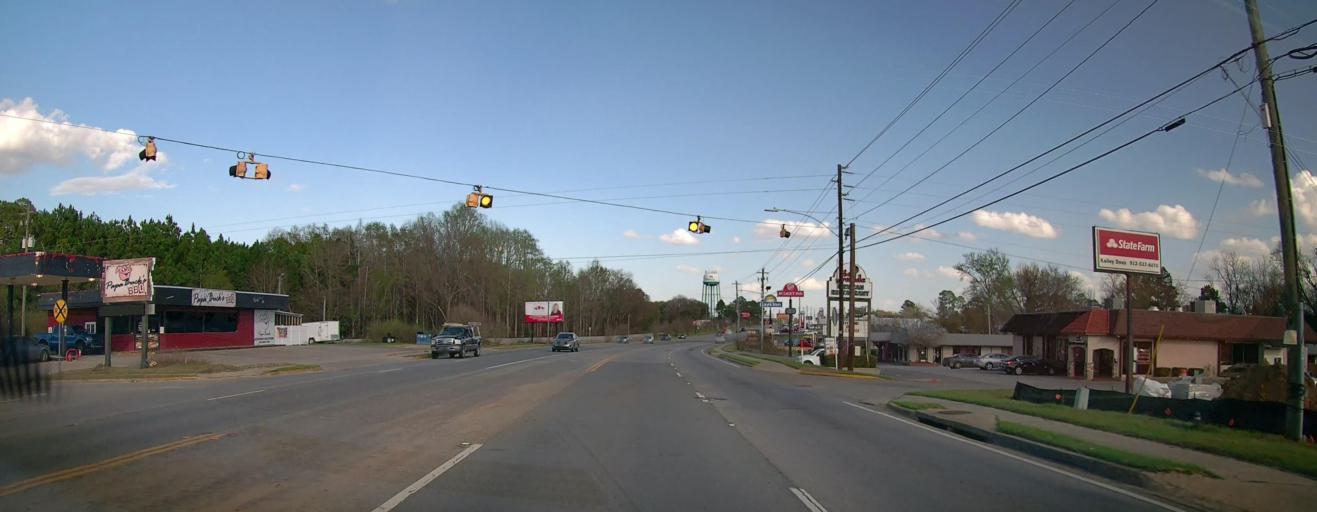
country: US
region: Georgia
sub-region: Toombs County
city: Vidalia
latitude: 32.2117
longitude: -82.3950
